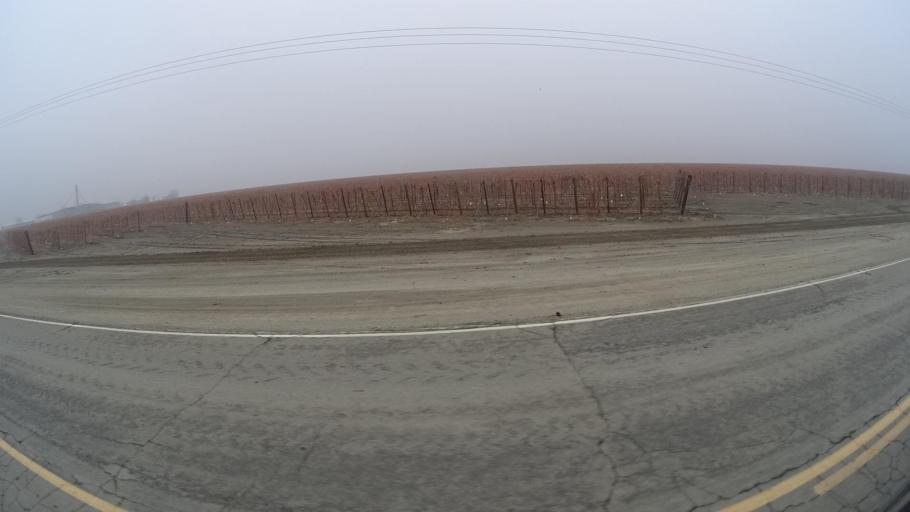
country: US
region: California
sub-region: Kern County
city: Buttonwillow
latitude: 35.4878
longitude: -119.5975
